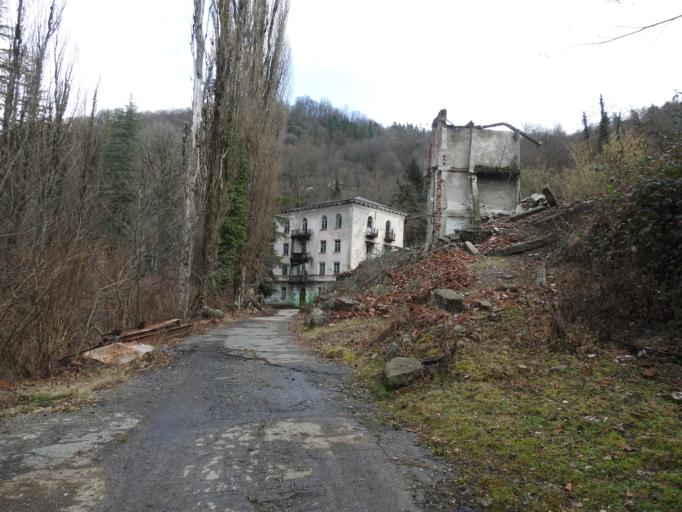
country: GE
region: Abkhazia
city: Tqvarch'eli
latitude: 42.8573
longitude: 41.7742
